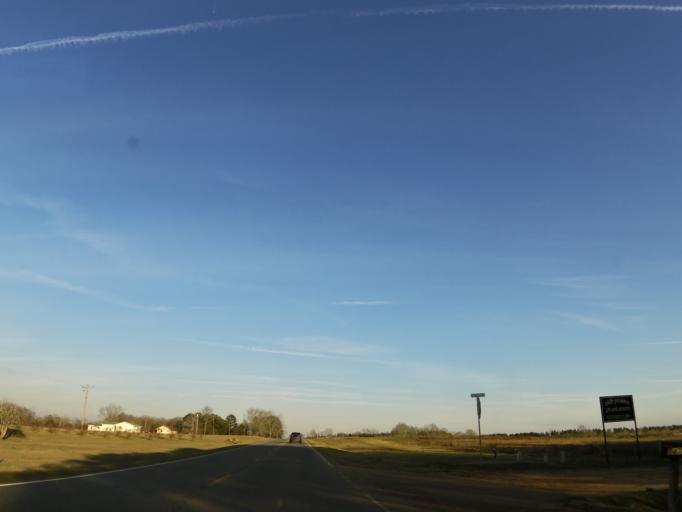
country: US
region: Georgia
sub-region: Sumter County
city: Americus
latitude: 32.0475
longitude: -84.3594
